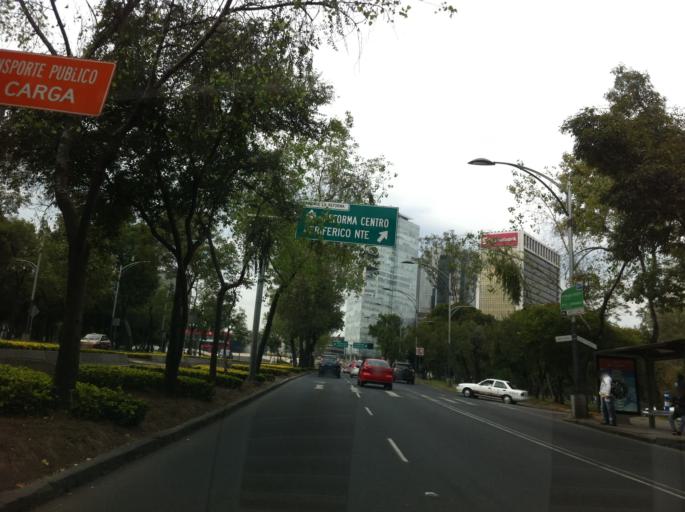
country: MX
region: Mexico City
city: Miguel Hidalgo
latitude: 19.4270
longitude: -99.1999
